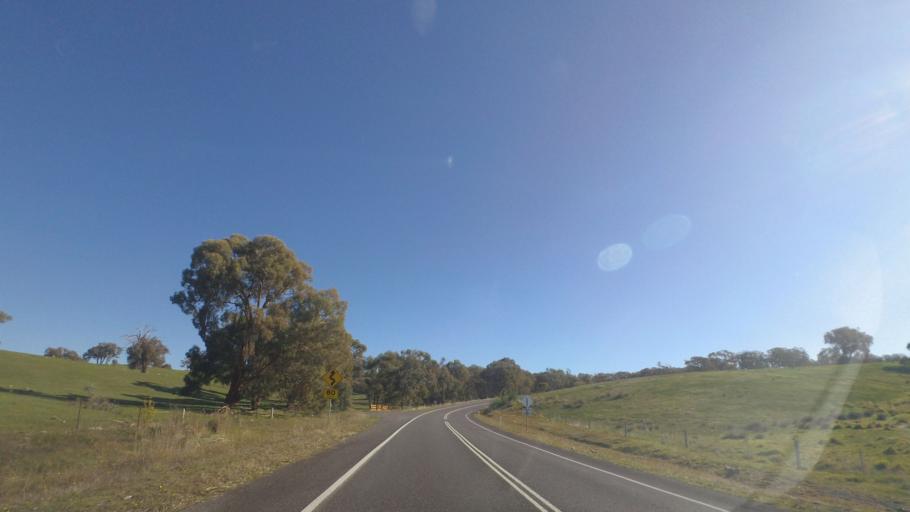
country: AU
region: Victoria
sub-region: Greater Bendigo
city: Kennington
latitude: -36.9129
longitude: 144.3306
